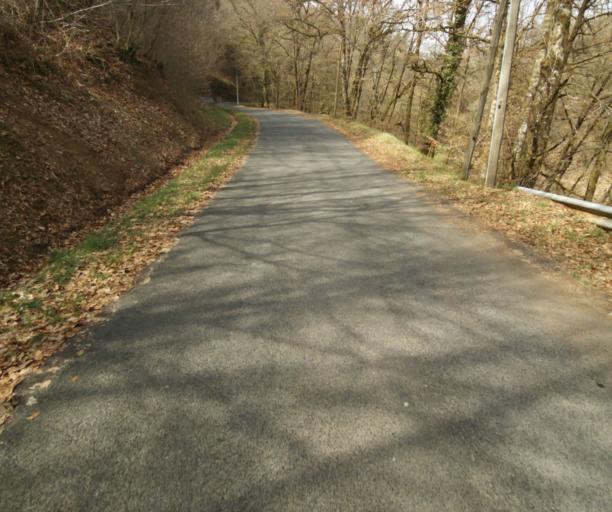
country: FR
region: Limousin
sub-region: Departement de la Correze
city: Naves
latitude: 45.3381
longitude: 1.7888
